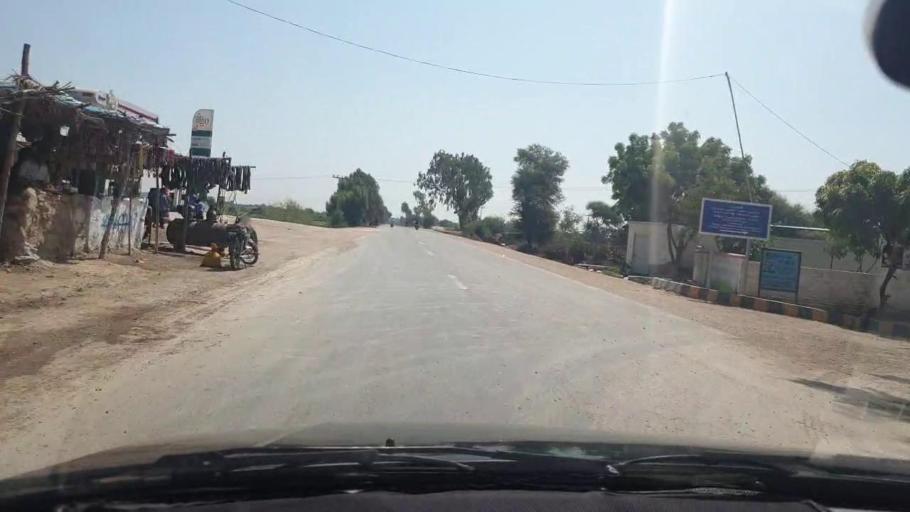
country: PK
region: Sindh
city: Tando Allahyar
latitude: 25.4334
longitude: 68.7447
